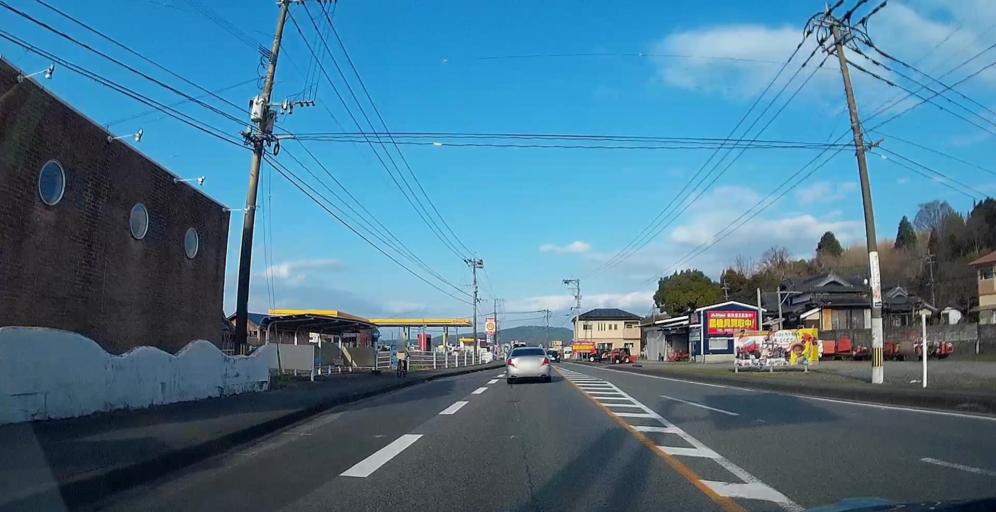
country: JP
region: Kumamoto
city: Matsubase
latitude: 32.5784
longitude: 130.6962
